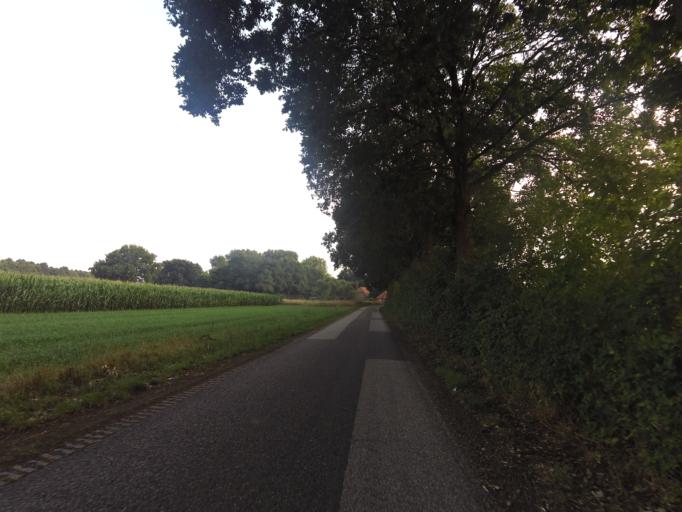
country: NL
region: Gelderland
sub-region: Oude IJsselstreek
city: Gendringen
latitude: 51.8688
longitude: 6.3870
